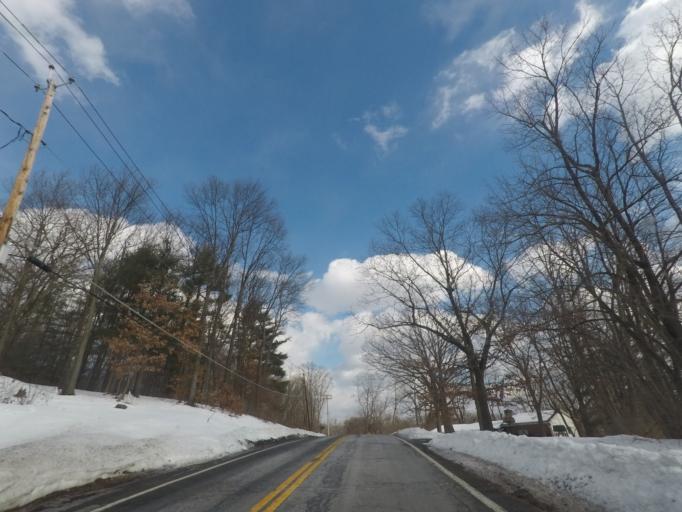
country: US
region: New York
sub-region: Albany County
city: Cohoes
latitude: 42.8101
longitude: -73.7531
